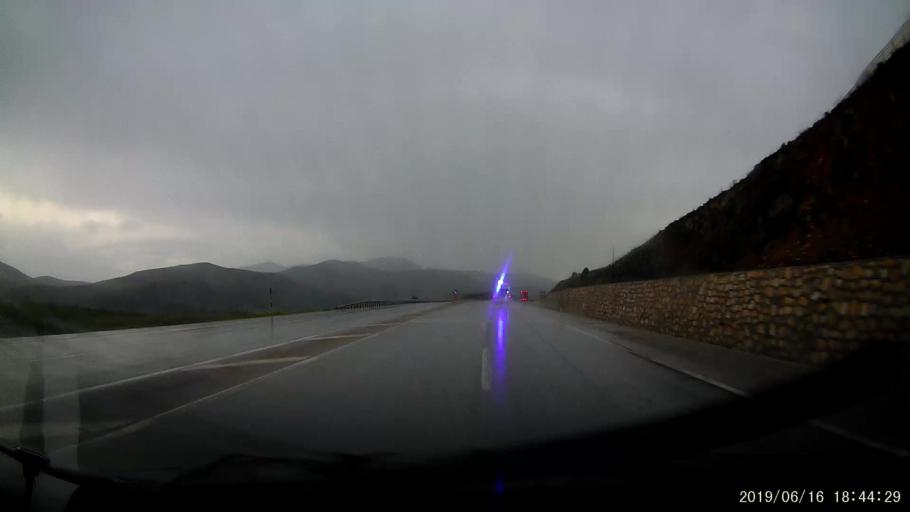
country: TR
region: Erzincan
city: Doganbeyli
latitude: 39.8693
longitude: 39.0718
